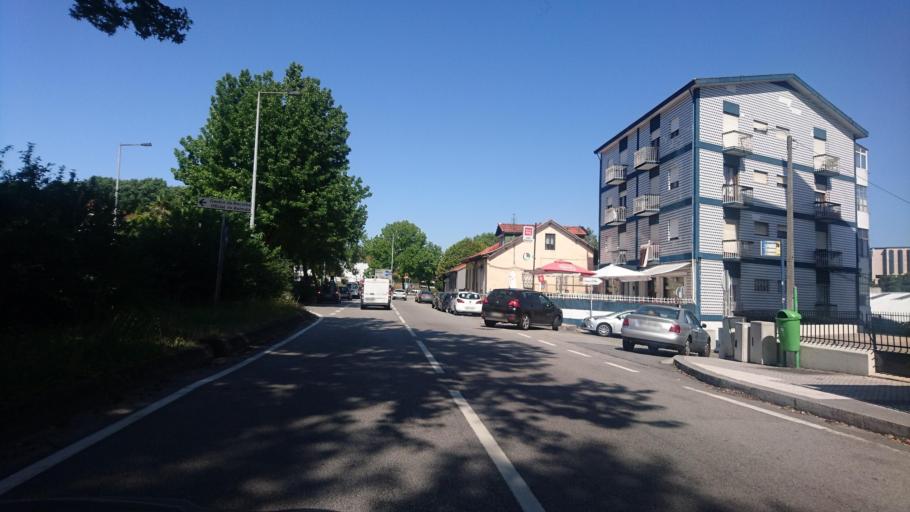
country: PT
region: Porto
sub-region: Gondomar
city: Rio Tinto
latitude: 41.1676
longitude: -8.5690
